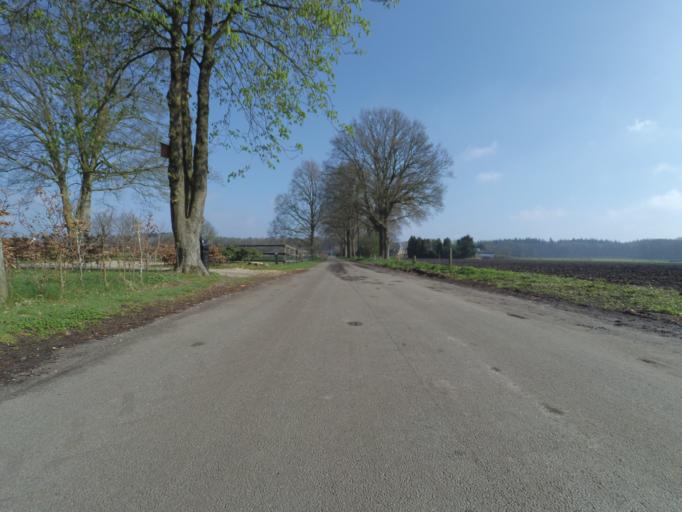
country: NL
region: Gelderland
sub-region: Gemeente Barneveld
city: Garderen
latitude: 52.2391
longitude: 5.7151
